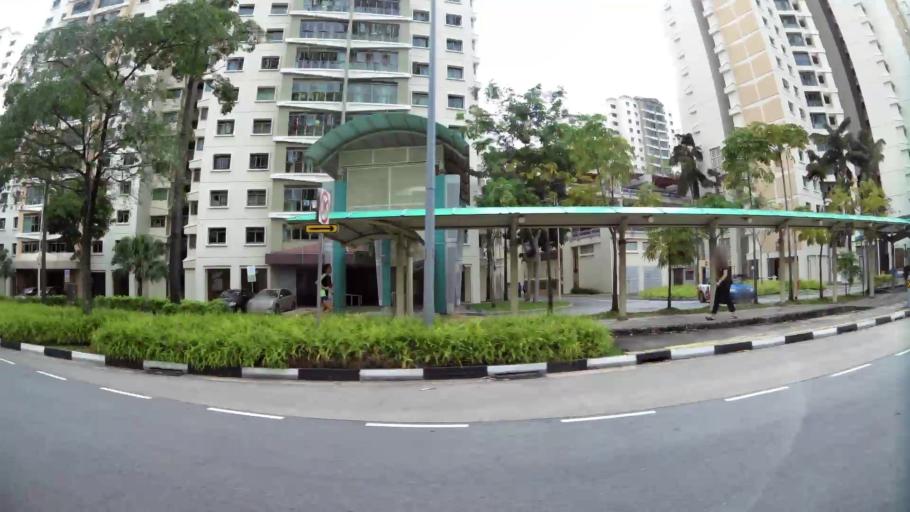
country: MY
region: Johor
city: Kampung Pasir Gudang Baru
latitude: 1.3965
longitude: 103.9151
